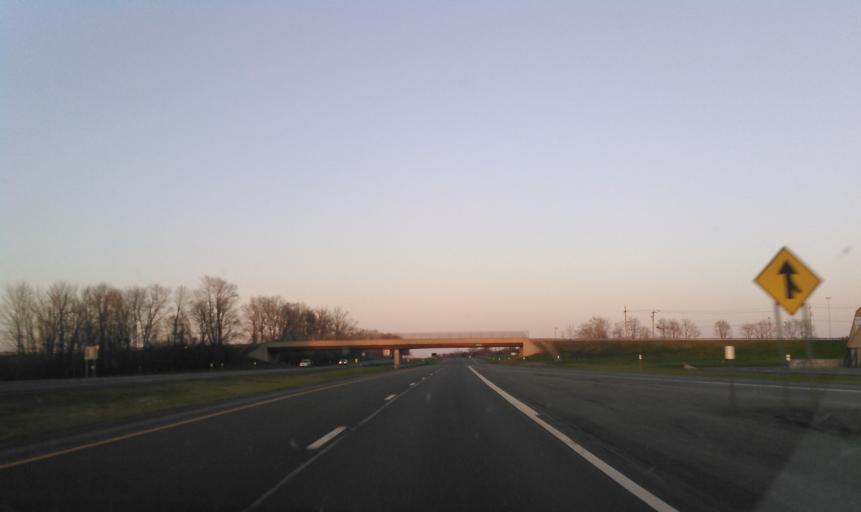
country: US
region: New York
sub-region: Seneca County
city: Waterloo
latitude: 42.9676
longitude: -76.8502
